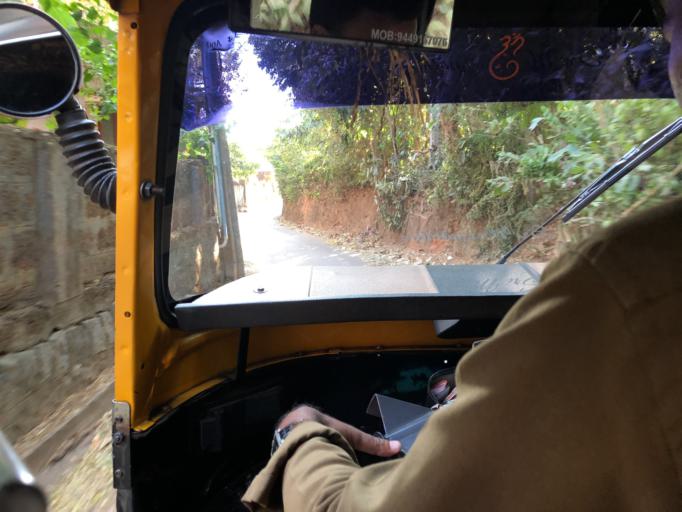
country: IN
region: Karnataka
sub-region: Dakshina Kannada
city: Mangalore
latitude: 12.9032
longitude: 74.8251
